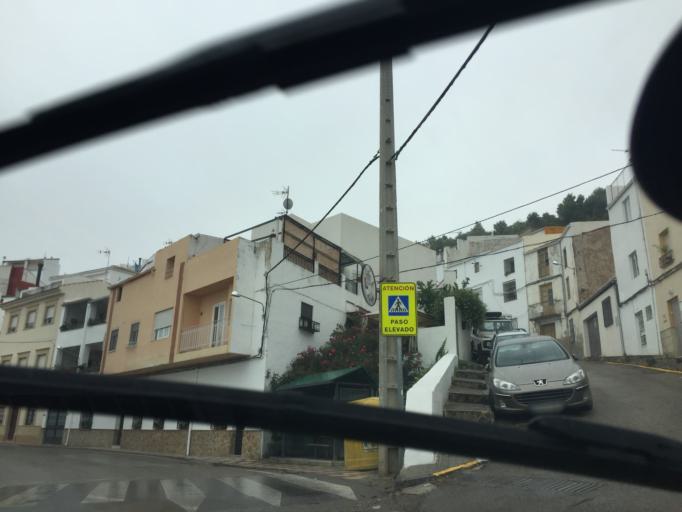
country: ES
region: Andalusia
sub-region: Provincia de Jaen
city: Jimena
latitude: 37.8400
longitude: -3.4744
